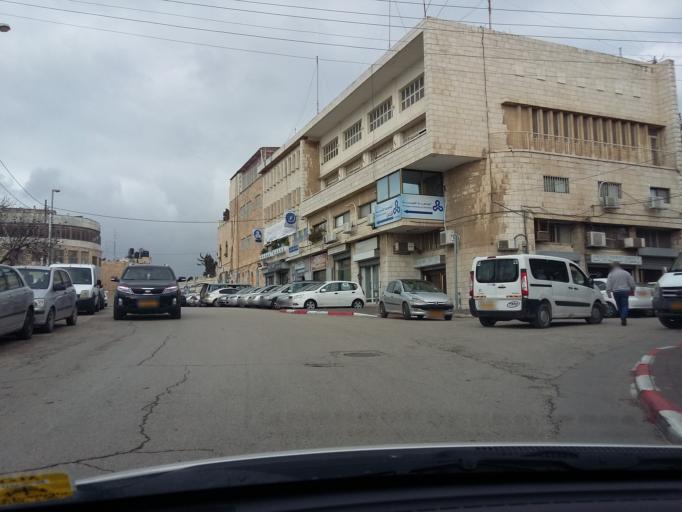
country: PS
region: West Bank
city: East Jerusalem
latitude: 31.7855
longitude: 35.2353
